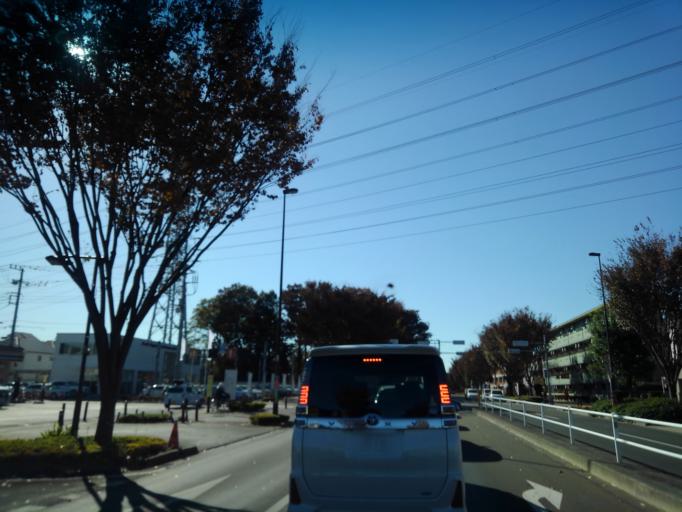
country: JP
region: Tokyo
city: Mitaka-shi
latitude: 35.6787
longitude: 139.5474
